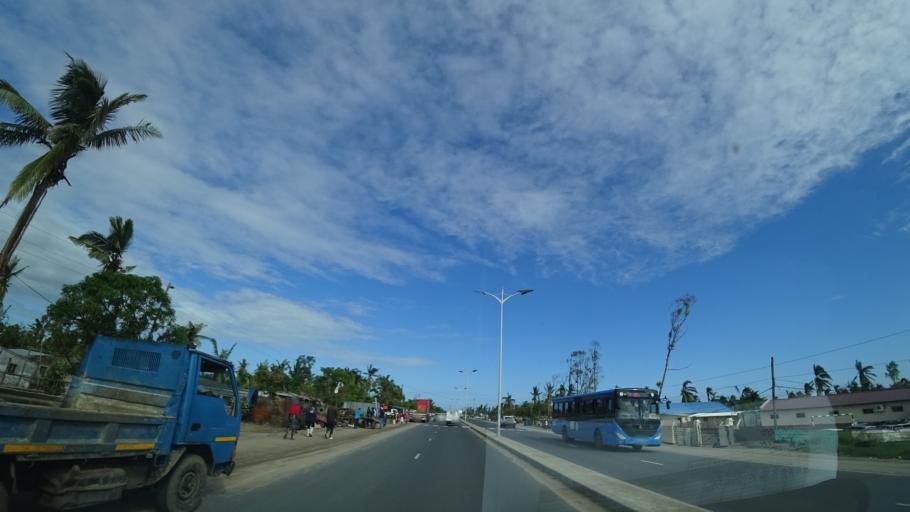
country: MZ
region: Sofala
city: Beira
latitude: -19.7591
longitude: 34.8787
